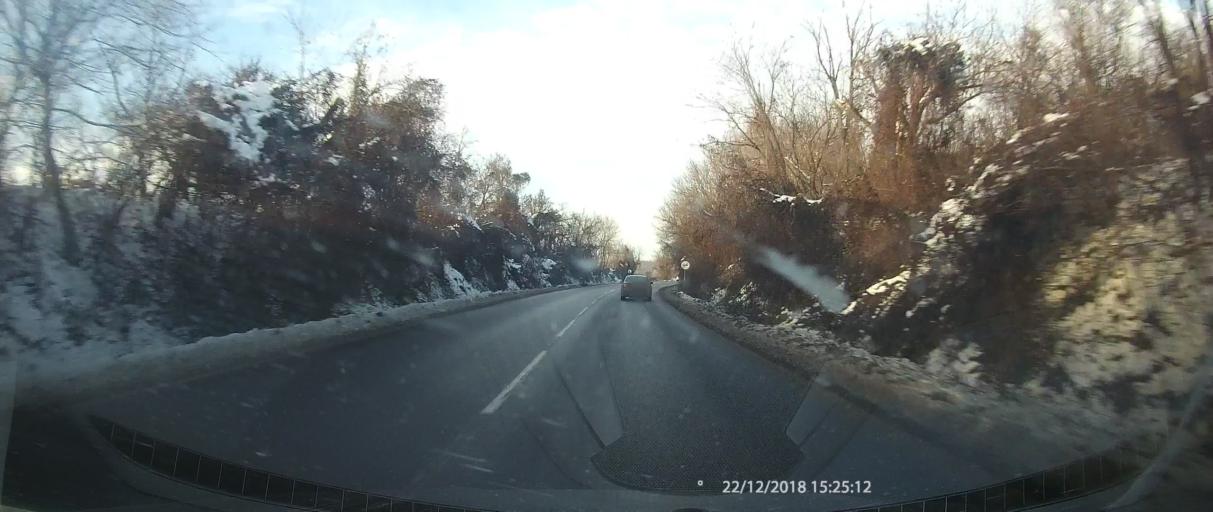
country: BG
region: Ruse
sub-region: Obshtina Ivanovo
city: Ivanovo
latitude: 43.7536
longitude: 25.9078
